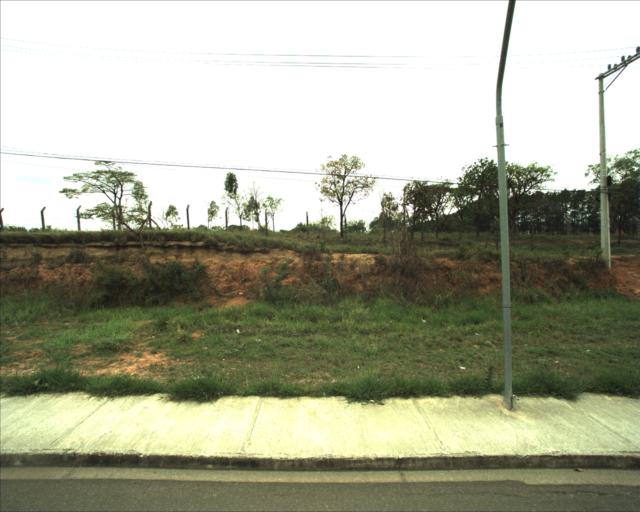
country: BR
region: Sao Paulo
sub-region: Sorocaba
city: Sorocaba
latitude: -23.4492
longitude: -47.3773
